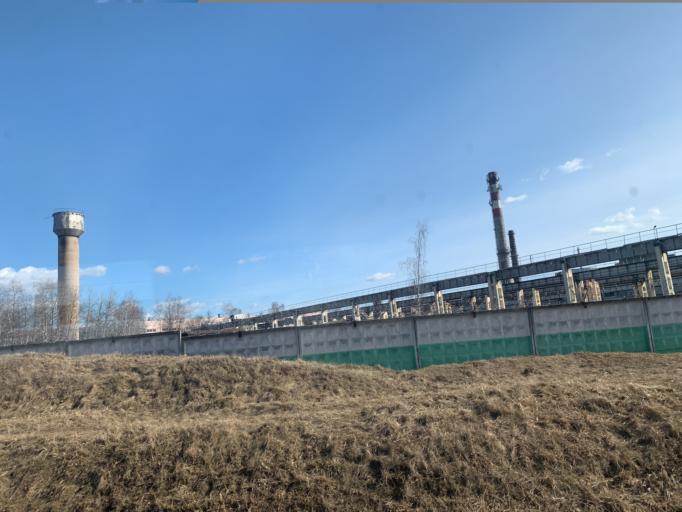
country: BY
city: Fanipol
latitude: 53.7410
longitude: 27.3258
